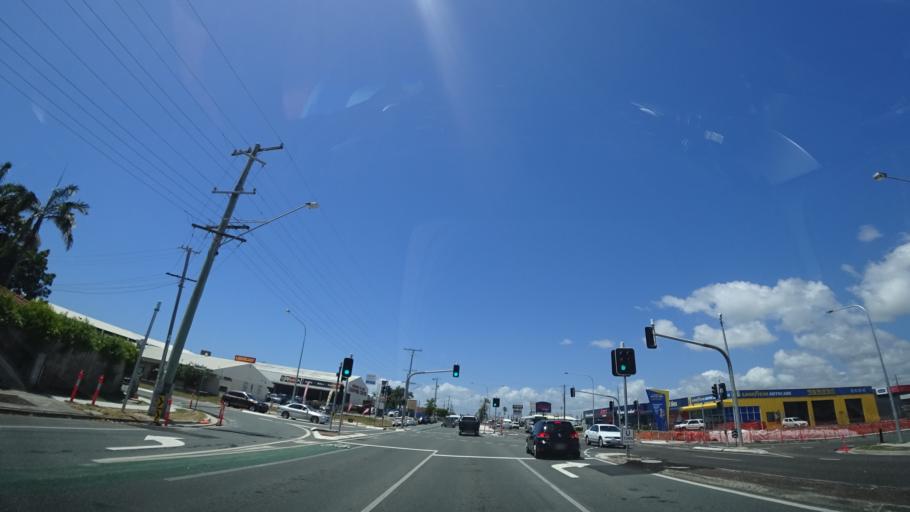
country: AU
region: Queensland
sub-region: Sunshine Coast
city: Mooloolaba
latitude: -26.7245
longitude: 153.1294
